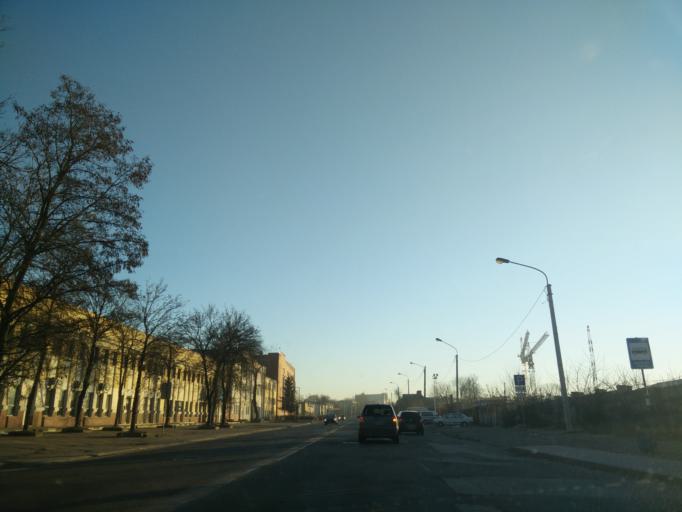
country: LT
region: Vilnius County
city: Vilkpede
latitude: 54.6680
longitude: 25.2554
